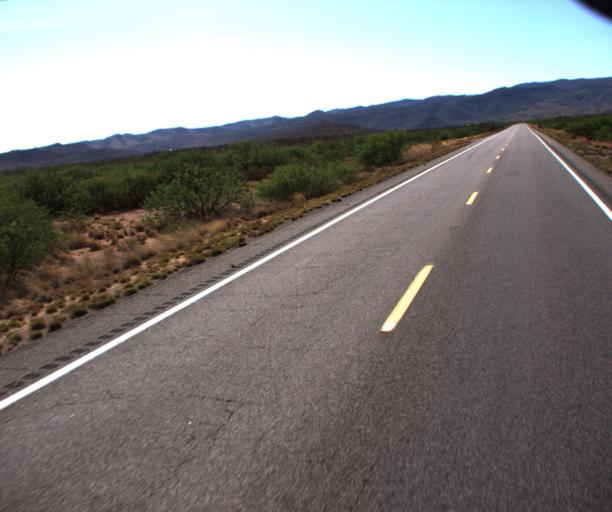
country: US
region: Arizona
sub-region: Cochise County
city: Bisbee
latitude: 31.5601
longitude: -110.0209
